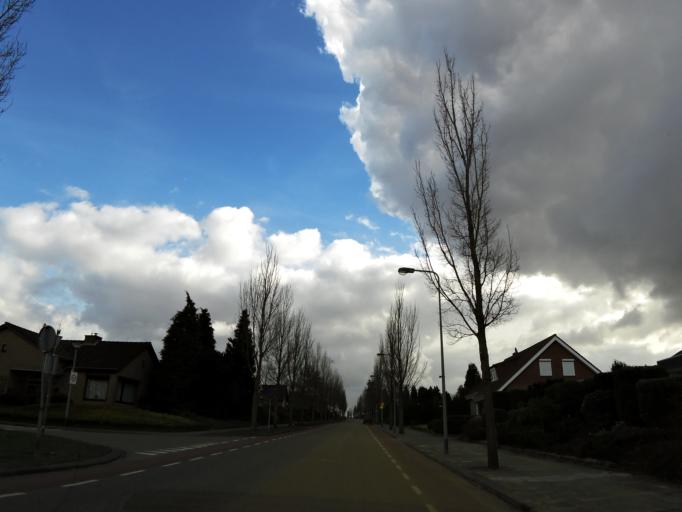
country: NL
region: Limburg
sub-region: Gemeente Brunssum
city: Brunssum
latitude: 50.9550
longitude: 5.9616
